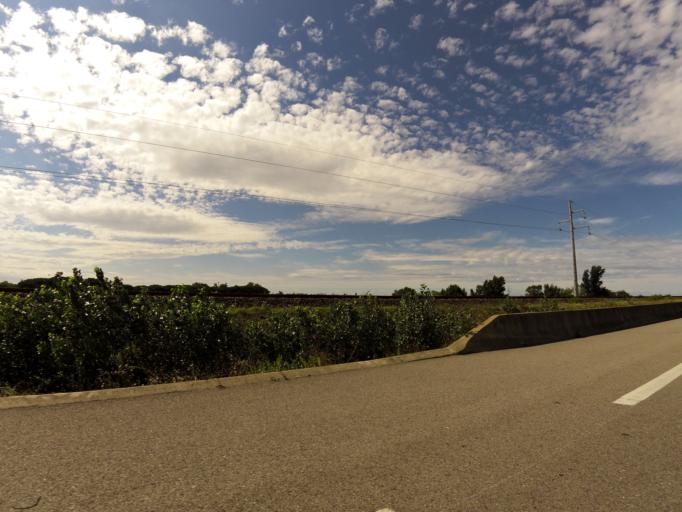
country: FR
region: Languedoc-Roussillon
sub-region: Departement du Gard
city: Aigues-Mortes
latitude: 43.5856
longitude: 4.1966
